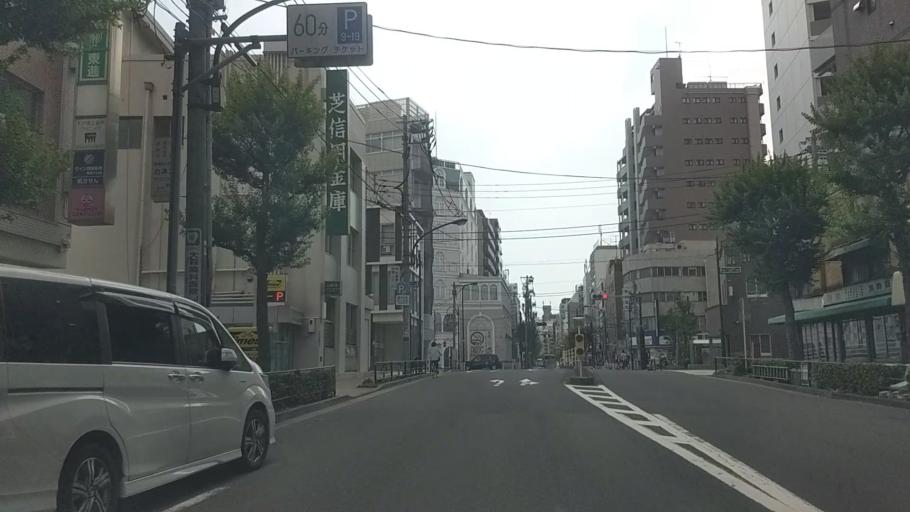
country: JP
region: Tokyo
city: Tokyo
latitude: 35.6202
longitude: 139.7025
